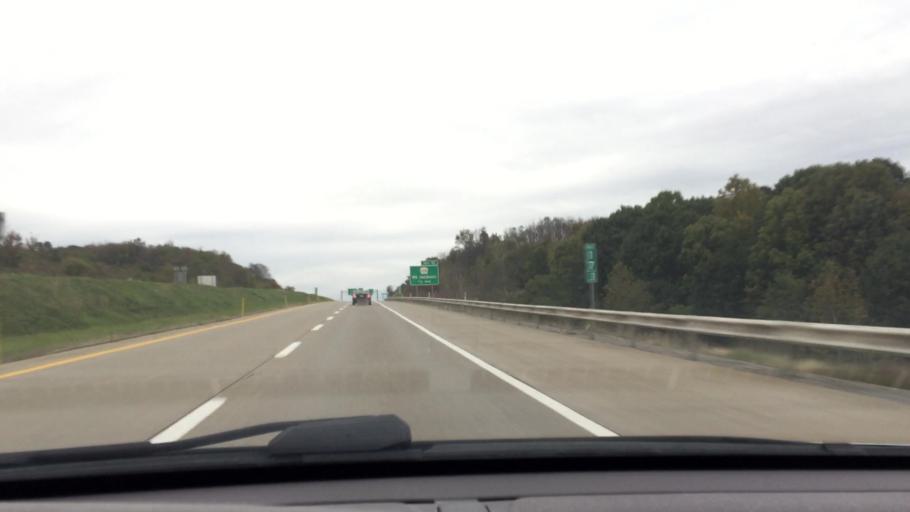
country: US
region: Pennsylvania
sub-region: Lawrence County
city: Oakland
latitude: 40.9591
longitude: -80.3955
